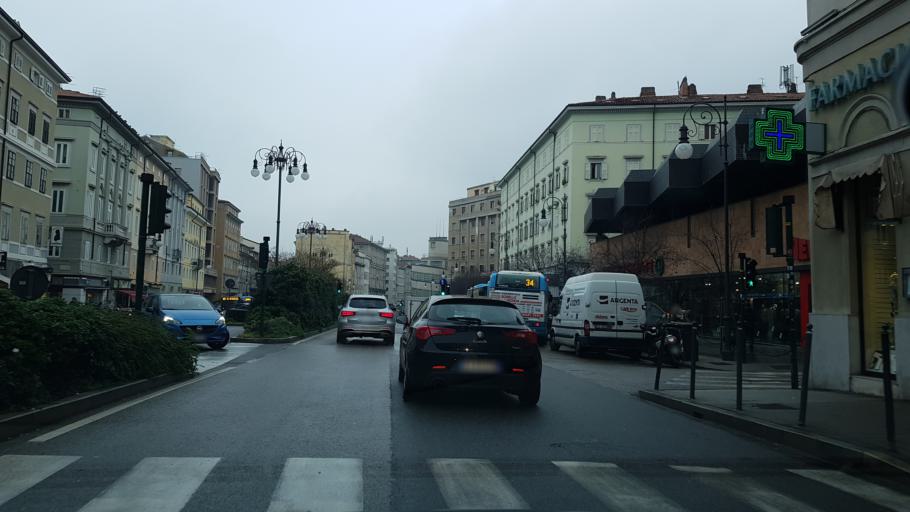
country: IT
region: Friuli Venezia Giulia
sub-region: Provincia di Trieste
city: Trieste
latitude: 45.6472
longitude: 13.7797
